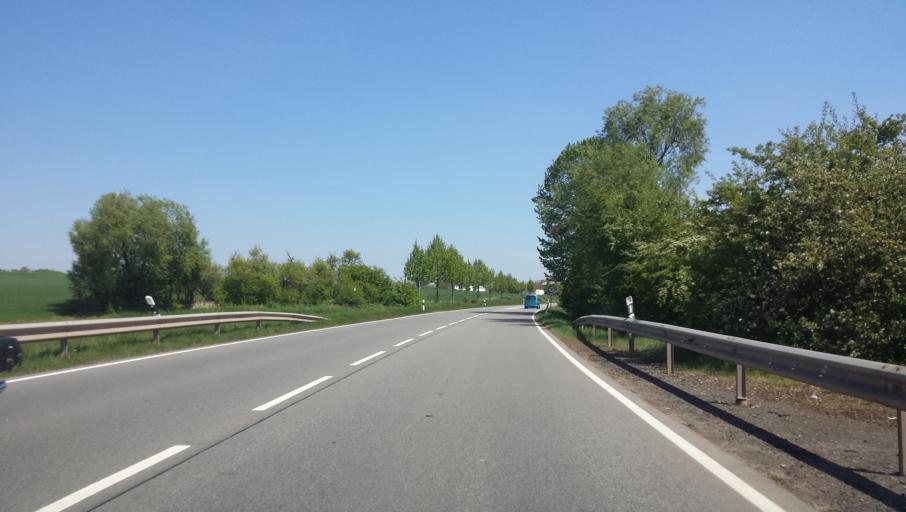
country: DE
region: Rheinland-Pfalz
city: Standenbuhl
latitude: 49.5937
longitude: 7.9732
